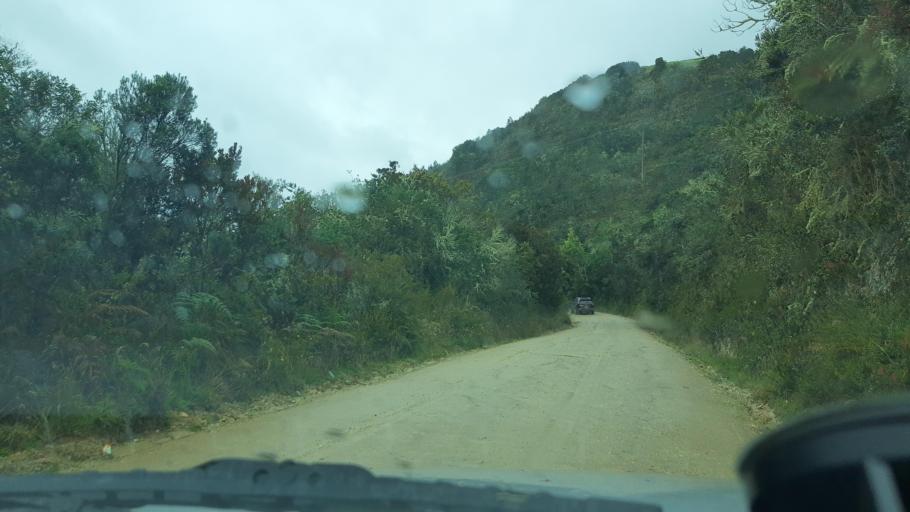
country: CO
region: Cundinamarca
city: Villapinzon
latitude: 5.2131
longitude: -73.5731
